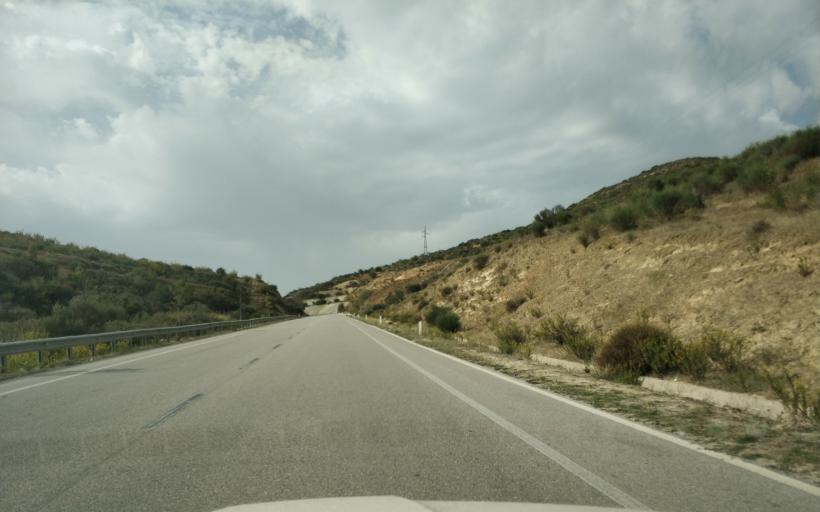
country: AL
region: Gjirokaster
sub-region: Rrethi i Tepelenes
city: Krahes
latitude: 40.3965
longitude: 19.8706
